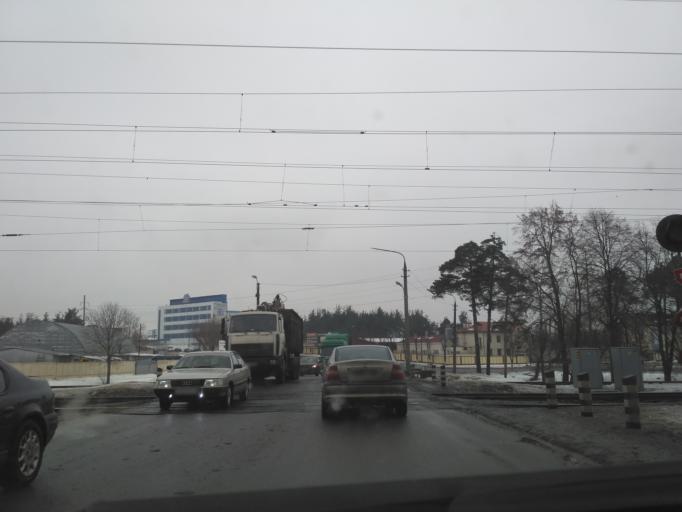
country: BY
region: Minsk
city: Horad Barysaw
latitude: 54.1968
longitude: 28.5152
